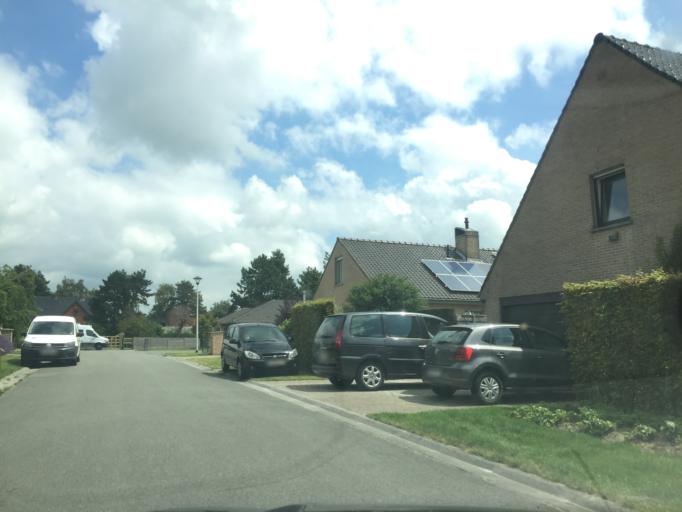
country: BE
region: Flanders
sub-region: Provincie West-Vlaanderen
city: Kortemark
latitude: 51.0369
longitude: 3.0405
